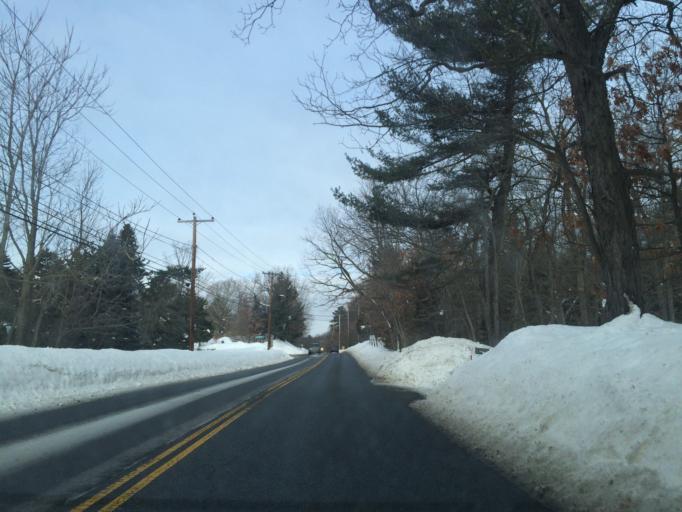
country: US
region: Massachusetts
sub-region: Middlesex County
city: Weston
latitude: 42.3389
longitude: -71.2910
